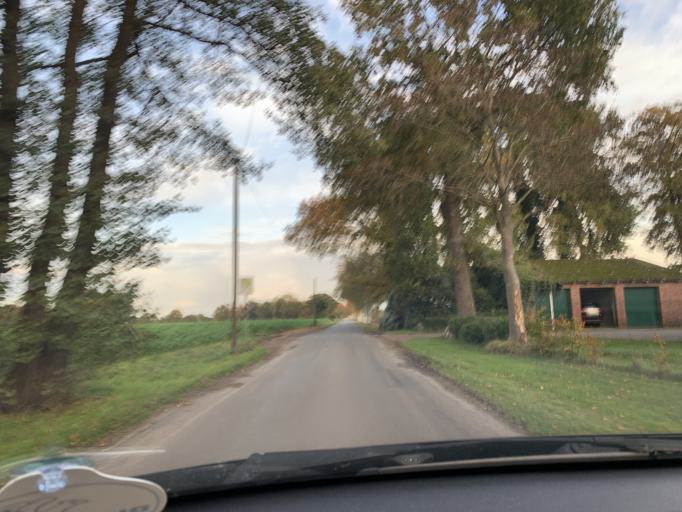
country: DE
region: Lower Saxony
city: Wiefelstede
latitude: 53.2523
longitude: 8.0795
